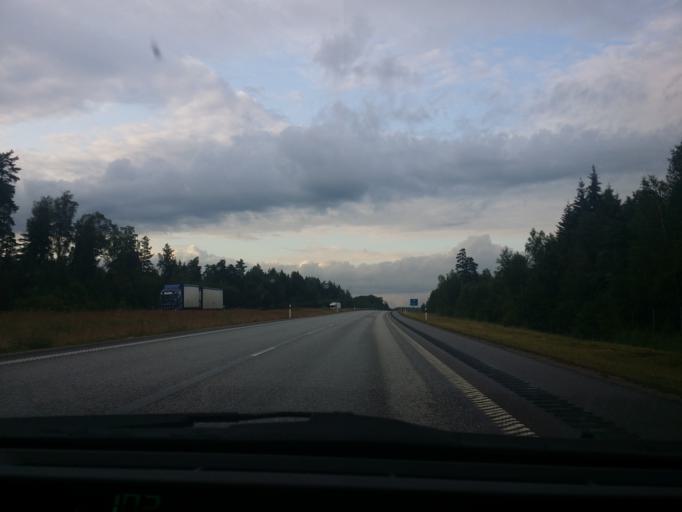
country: SE
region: Vaestmanland
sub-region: Kopings Kommun
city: Koping
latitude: 59.4897
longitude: 15.9175
